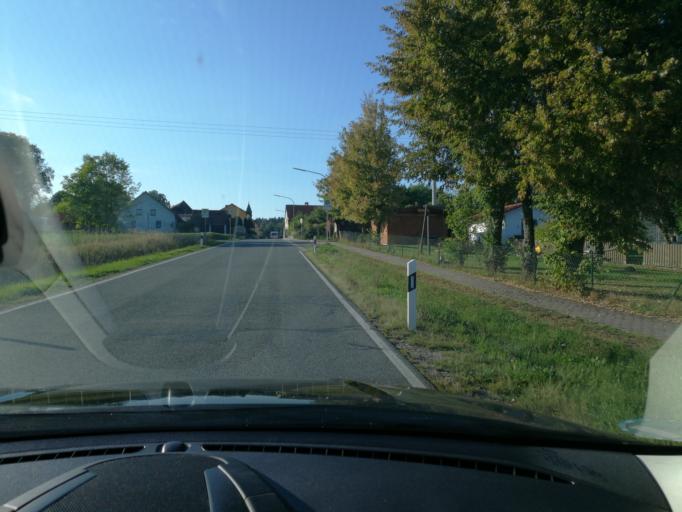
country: DE
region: Bavaria
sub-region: Upper Palatinate
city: Hohenfels
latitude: 49.1849
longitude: 11.8148
